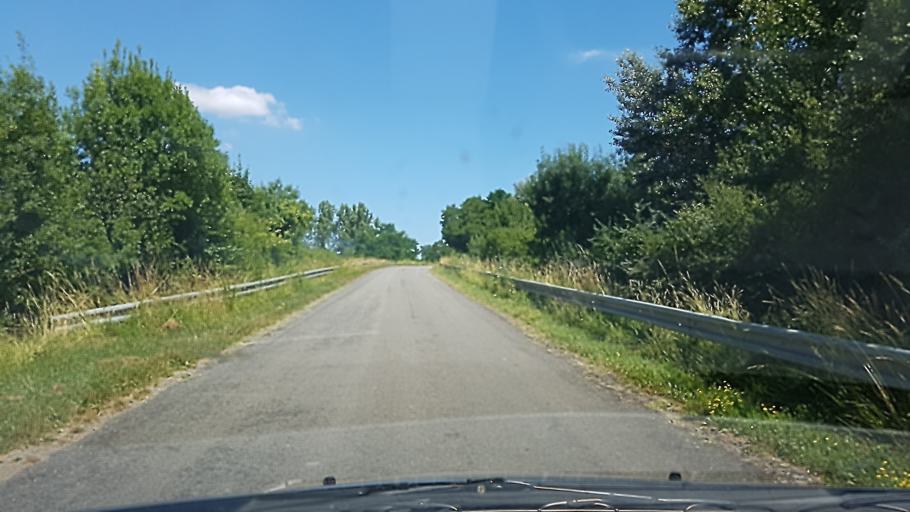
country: FR
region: Pays de la Loire
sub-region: Departement de Maine-et-Loire
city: Le Plessis-Grammoire
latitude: 47.5158
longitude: -0.4077
